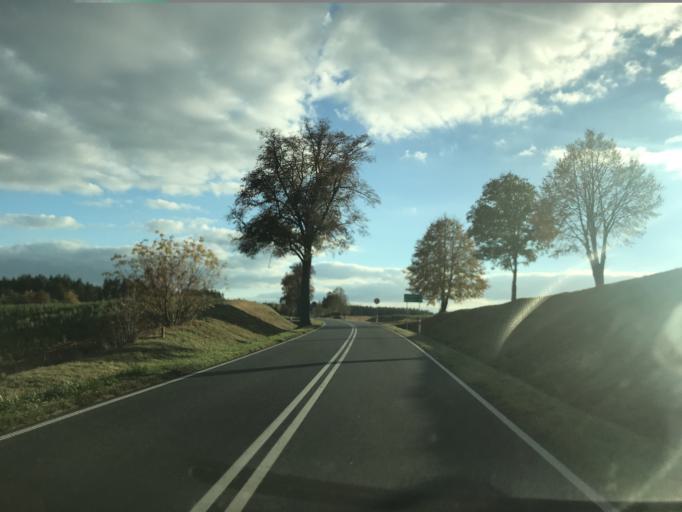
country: PL
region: Warmian-Masurian Voivodeship
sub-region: Powiat dzialdowski
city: Lidzbark
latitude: 53.3413
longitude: 19.8188
